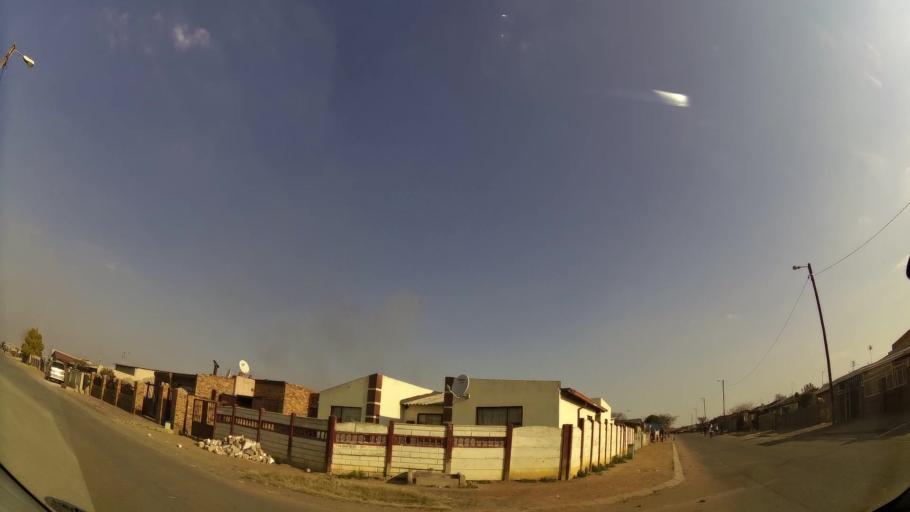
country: ZA
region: Gauteng
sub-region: Ekurhuleni Metropolitan Municipality
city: Brakpan
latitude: -26.1448
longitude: 28.4176
